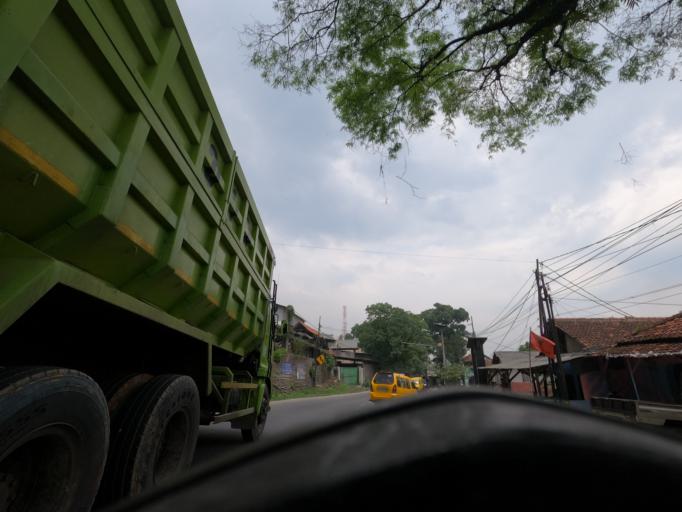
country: ID
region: West Java
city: Padalarang
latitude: -6.8311
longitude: 107.4316
